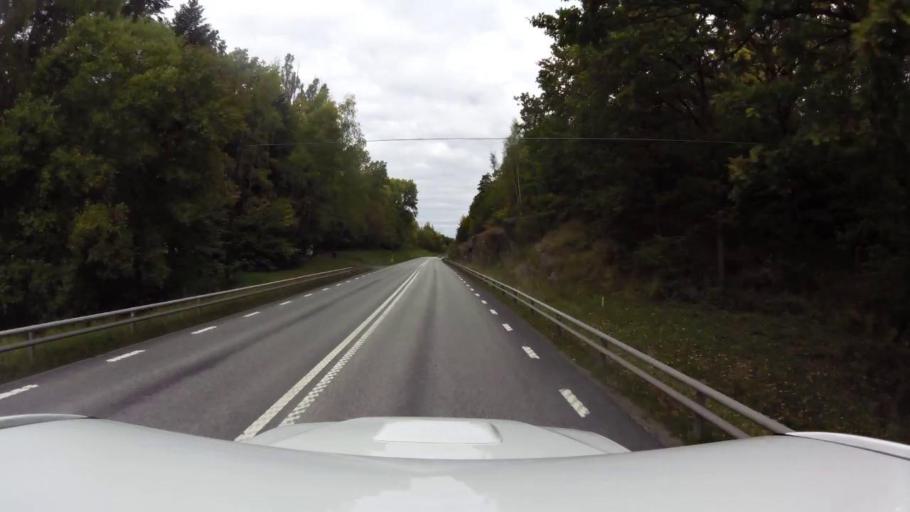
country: SE
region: OEstergoetland
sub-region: Kinda Kommun
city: Rimforsa
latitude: 58.1844
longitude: 15.6704
